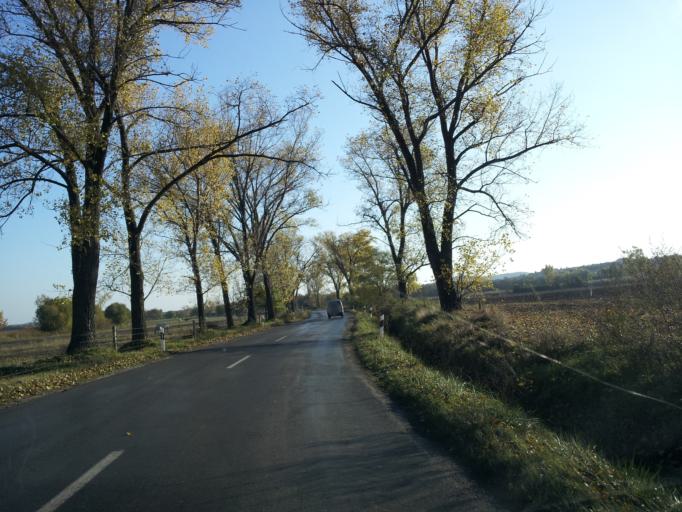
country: HU
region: Fejer
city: Fehervarcsurgo
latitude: 47.3054
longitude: 18.2553
